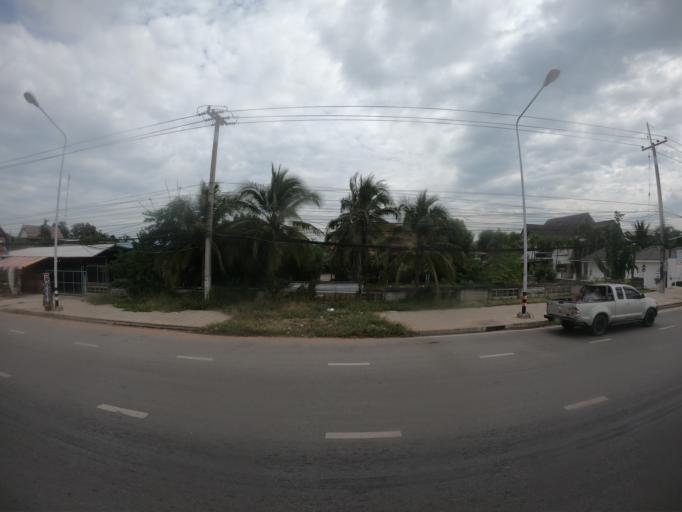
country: TH
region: Maha Sarakham
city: Kantharawichai
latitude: 16.3209
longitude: 103.2992
